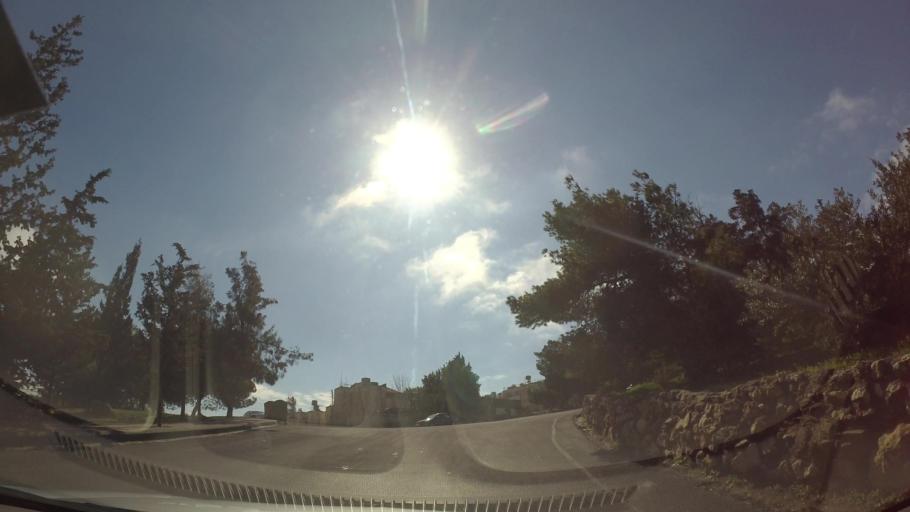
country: JO
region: Amman
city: Al Jubayhah
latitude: 32.0585
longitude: 35.8803
